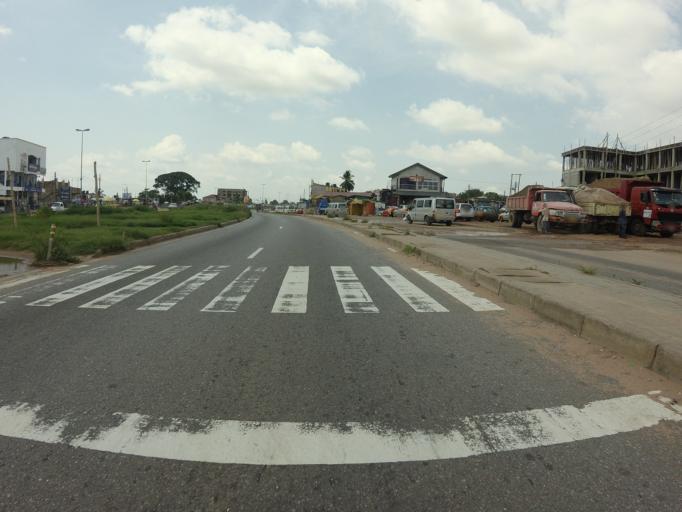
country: GH
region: Greater Accra
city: Gbawe
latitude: 5.6271
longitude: -0.3094
